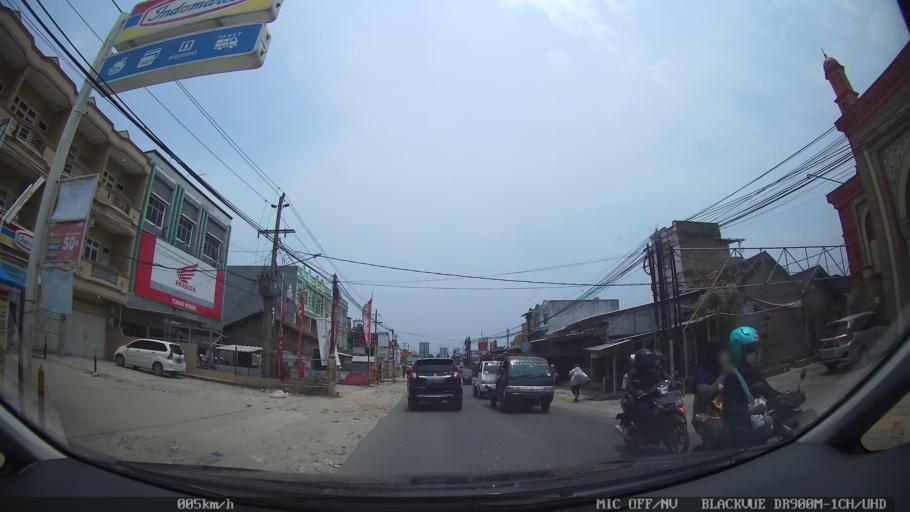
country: ID
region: Lampung
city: Kedaton
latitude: -5.3958
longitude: 105.2992
